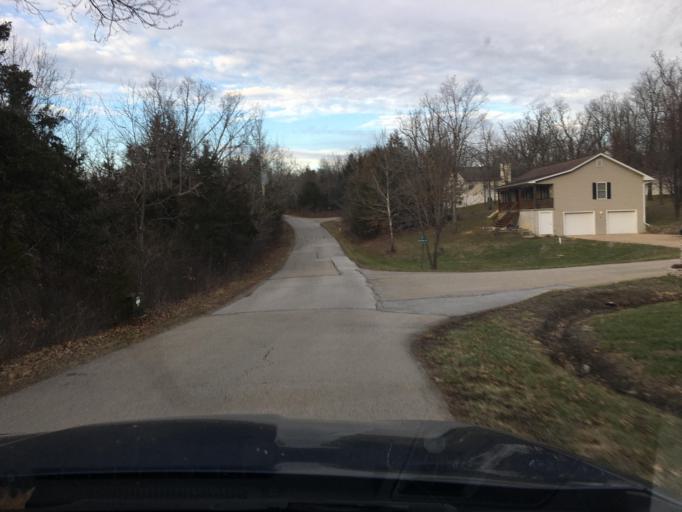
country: US
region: Missouri
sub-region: Jefferson County
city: De Soto
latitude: 38.0921
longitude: -90.5664
